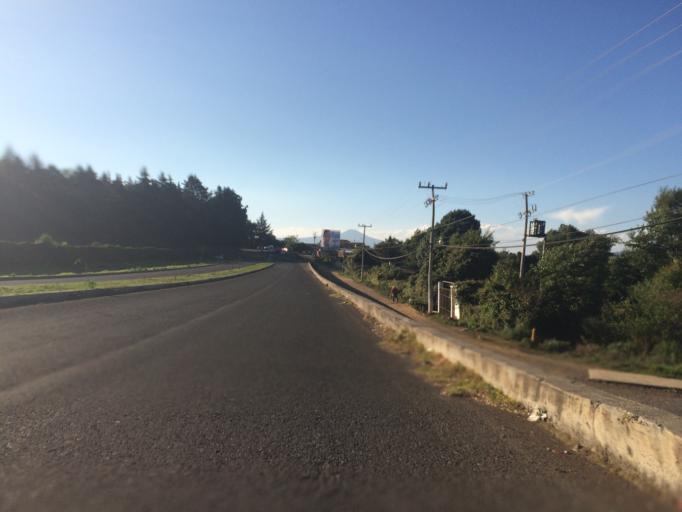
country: MX
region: Michoacan
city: Patzcuaro
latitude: 19.5036
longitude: -101.6038
